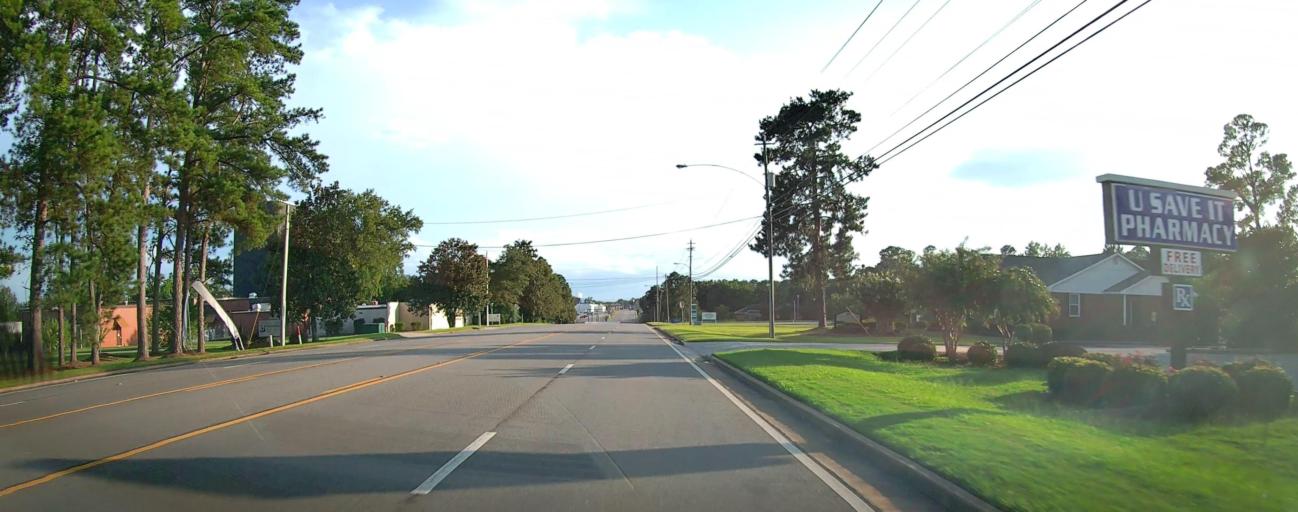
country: US
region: Georgia
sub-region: Peach County
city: Fort Valley
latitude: 32.5665
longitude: -83.8762
